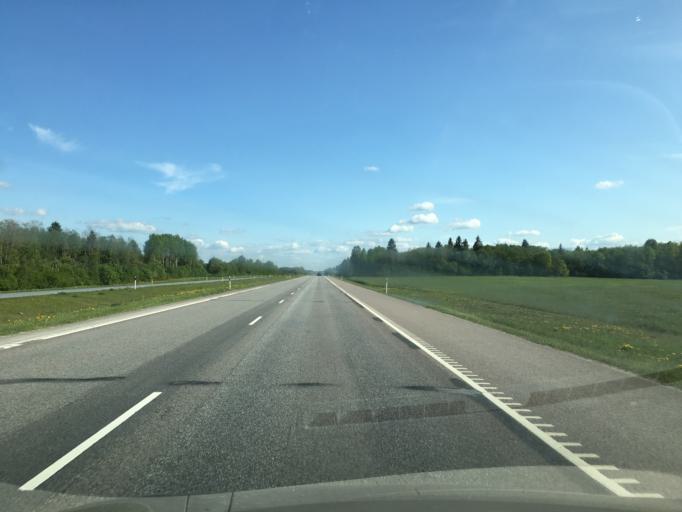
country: EE
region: Harju
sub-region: Rae vald
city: Vaida
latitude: 59.2728
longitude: 24.9880
